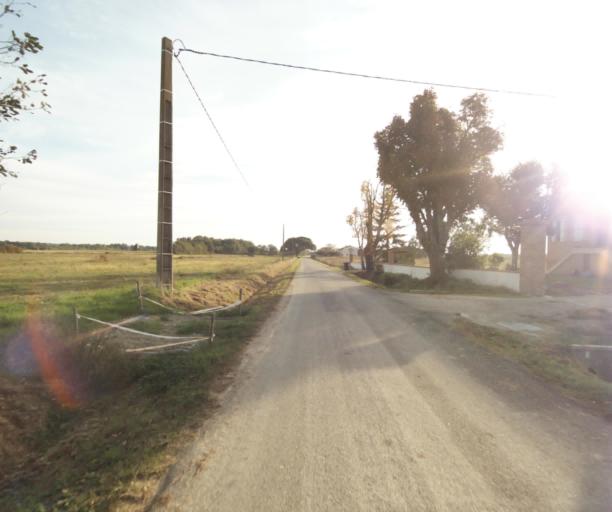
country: FR
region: Midi-Pyrenees
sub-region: Departement du Tarn-et-Garonne
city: Labastide-Saint-Pierre
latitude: 43.8955
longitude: 1.3580
